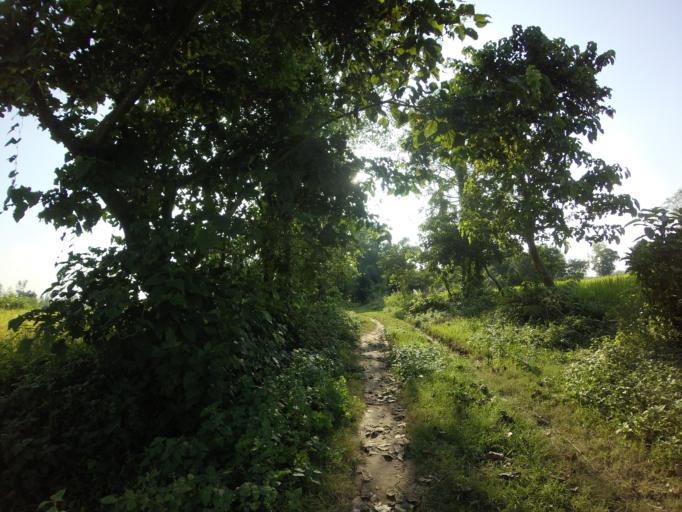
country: NP
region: Far Western
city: Tikapur
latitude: 28.4453
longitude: 81.0764
